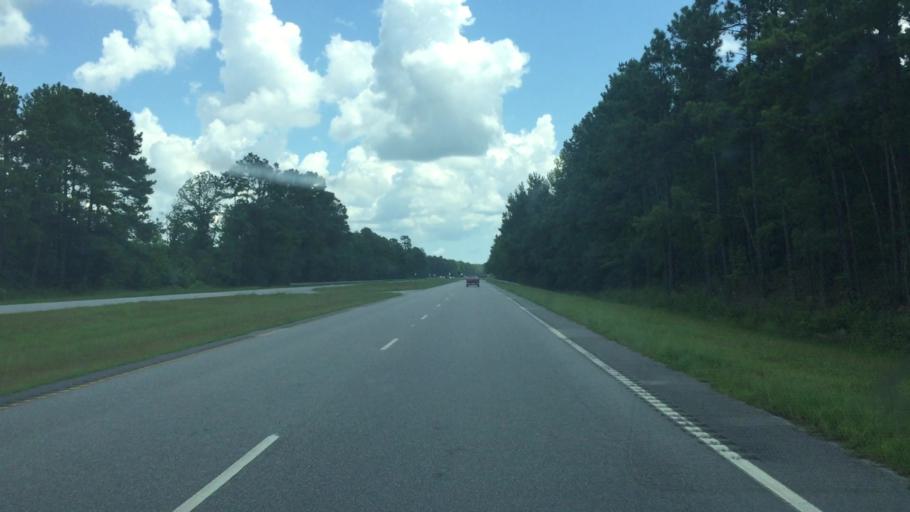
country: US
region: South Carolina
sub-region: Horry County
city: Loris
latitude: 34.0379
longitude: -78.8161
